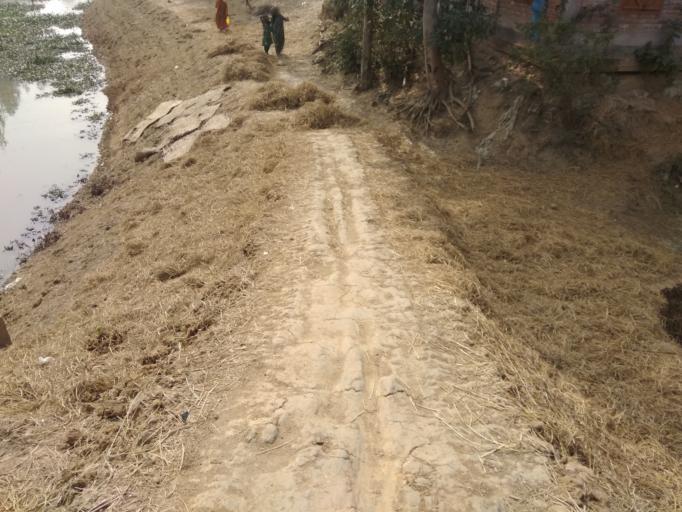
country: BD
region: Rajshahi
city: Ishurdi
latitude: 24.4655
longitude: 89.2668
